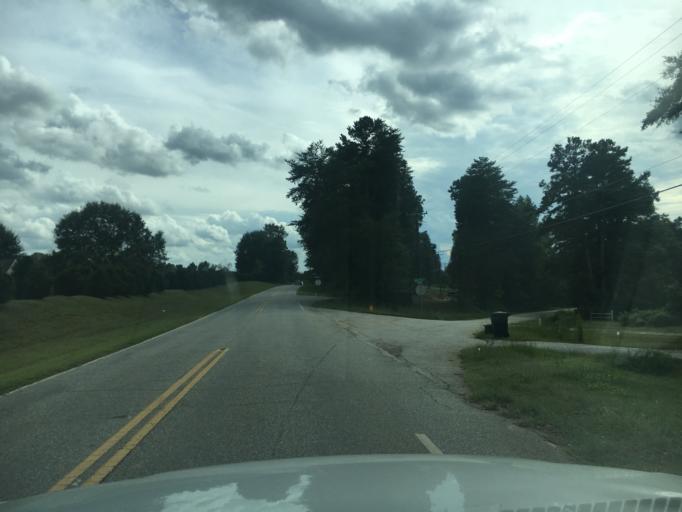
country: US
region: South Carolina
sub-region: Spartanburg County
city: Fairforest
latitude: 34.9054
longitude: -82.0521
